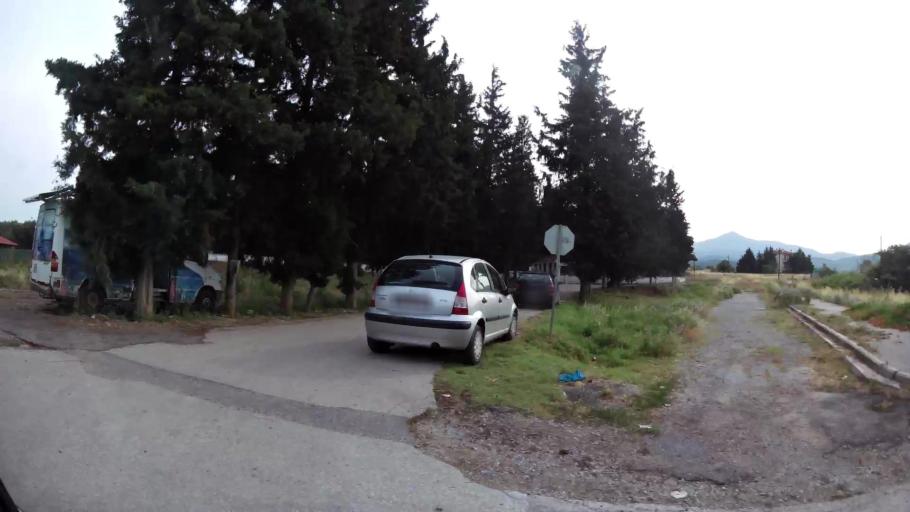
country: GR
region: Central Macedonia
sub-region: Nomos Thessalonikis
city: Thermi
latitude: 40.5523
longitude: 23.0239
